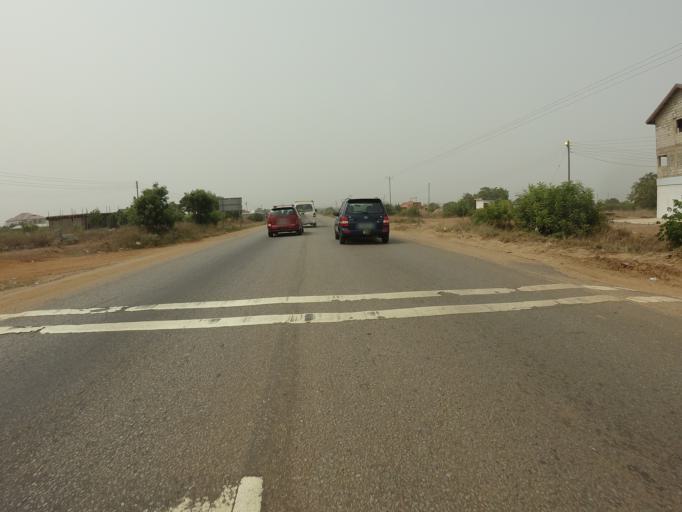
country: GH
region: Greater Accra
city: Tema
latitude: 5.8339
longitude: 0.2155
